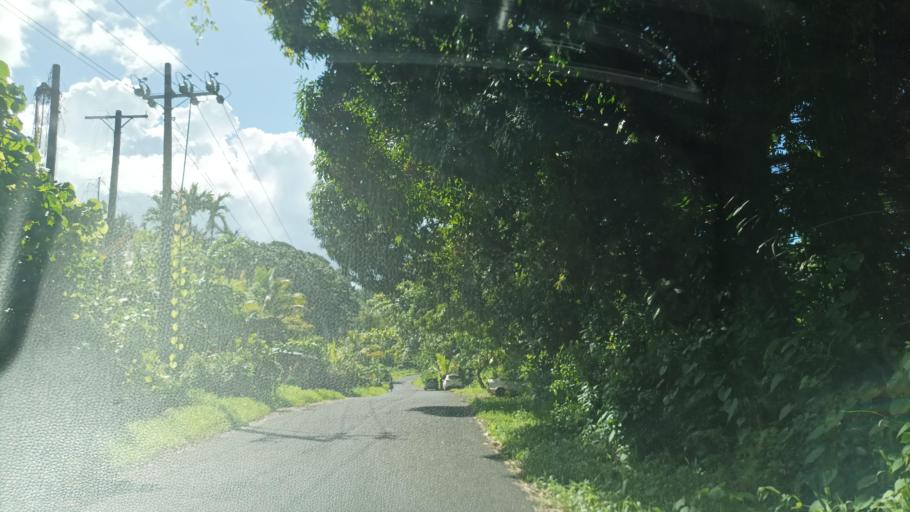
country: FM
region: Pohnpei
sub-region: Madolenihm Municipality
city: Madolenihm Municipality Government
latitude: 6.8497
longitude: 158.2993
